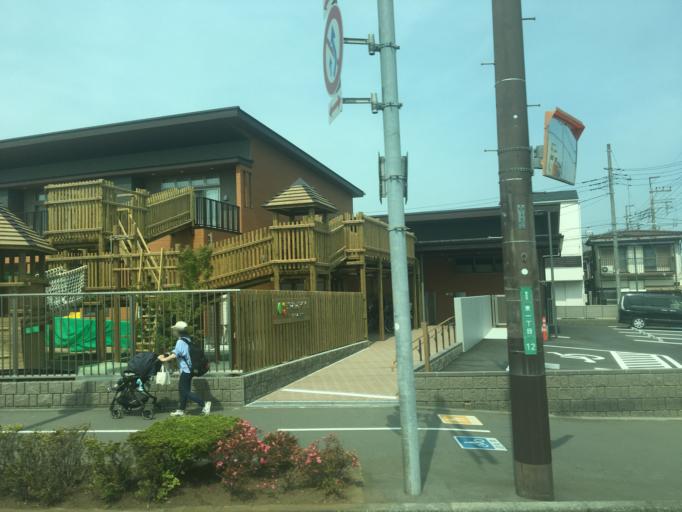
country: JP
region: Saitama
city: Shiki
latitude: 35.8110
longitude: 139.5710
